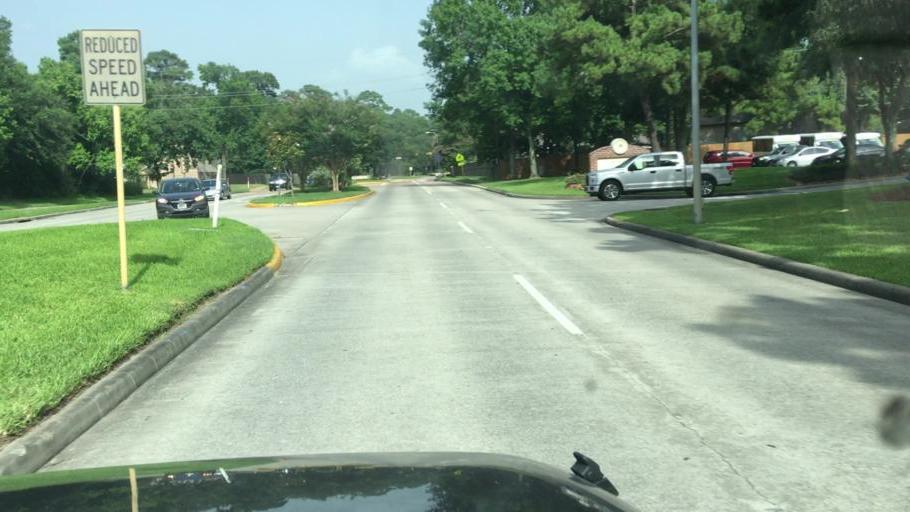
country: US
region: Texas
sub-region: Harris County
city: Atascocita
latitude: 30.0080
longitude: -95.1709
